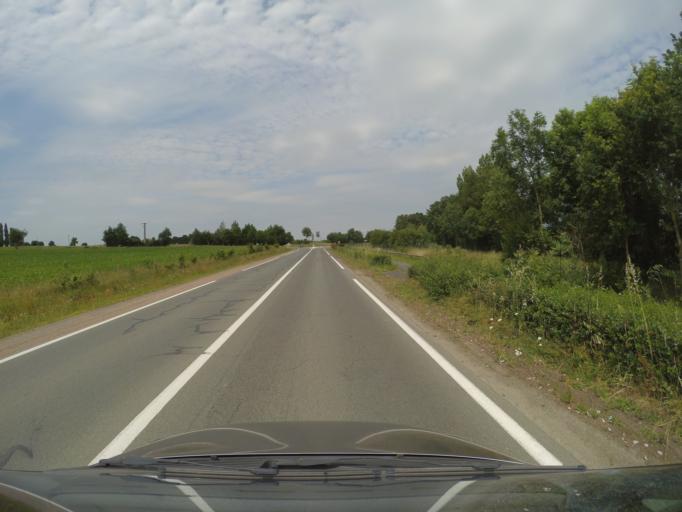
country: FR
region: Pays de la Loire
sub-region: Departement de la Vendee
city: Les Herbiers
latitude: 46.8453
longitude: -1.0133
